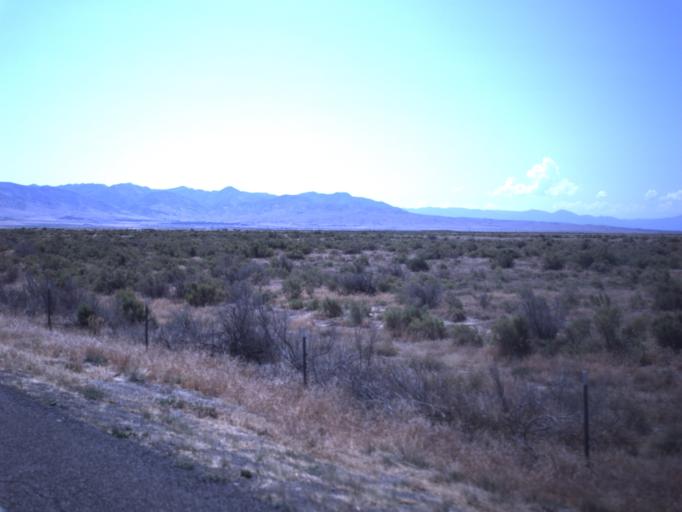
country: US
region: Utah
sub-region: Millard County
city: Delta
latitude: 39.4705
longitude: -112.4617
